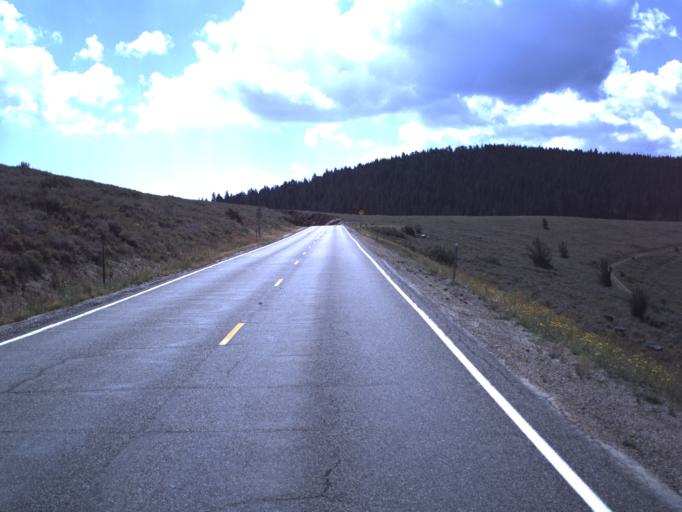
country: US
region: Idaho
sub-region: Bear Lake County
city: Paris
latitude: 41.9546
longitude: -111.4979
